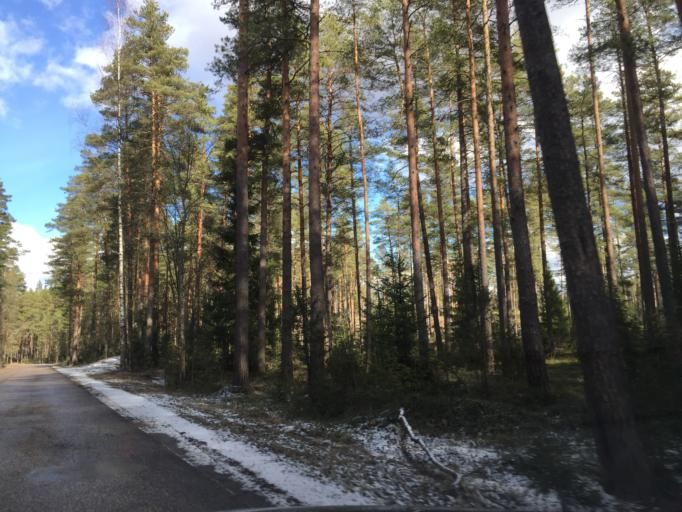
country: LV
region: Garkalne
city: Garkalne
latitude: 56.9568
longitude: 24.4364
